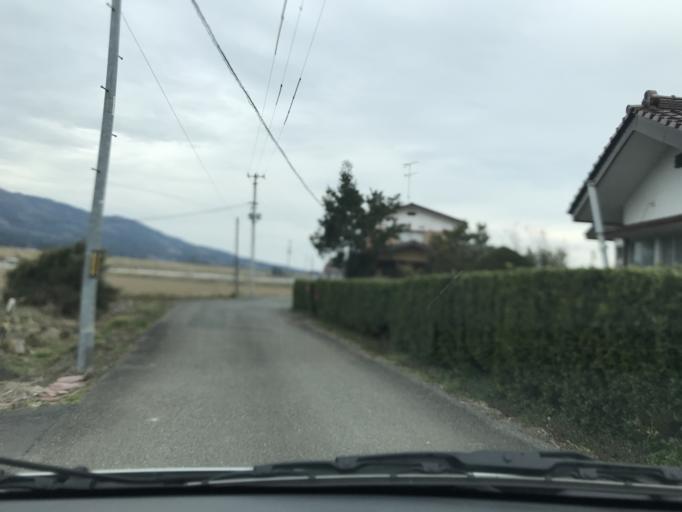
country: JP
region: Iwate
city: Mizusawa
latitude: 39.0598
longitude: 141.1527
